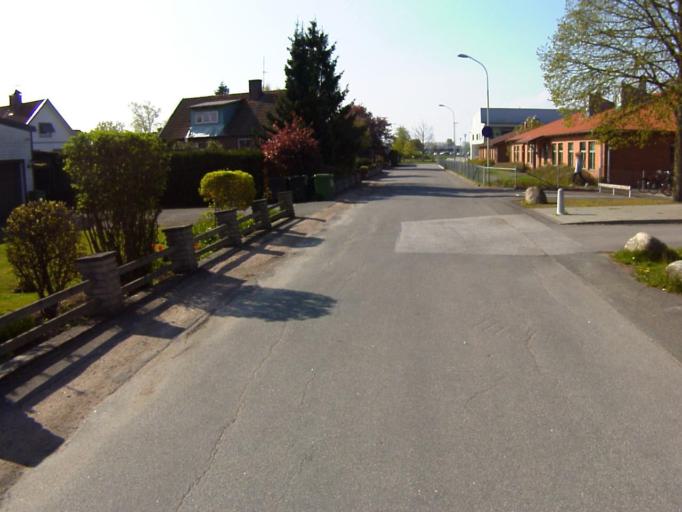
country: SE
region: Skane
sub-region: Kristianstads Kommun
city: Kristianstad
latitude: 56.0316
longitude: 14.2092
